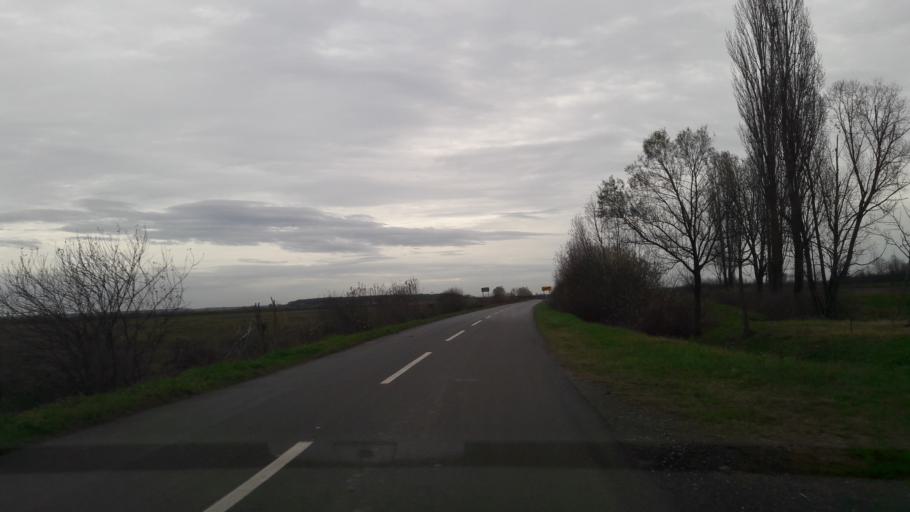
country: HR
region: Virovitick-Podravska
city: Zdenci
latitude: 45.6087
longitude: 18.0179
